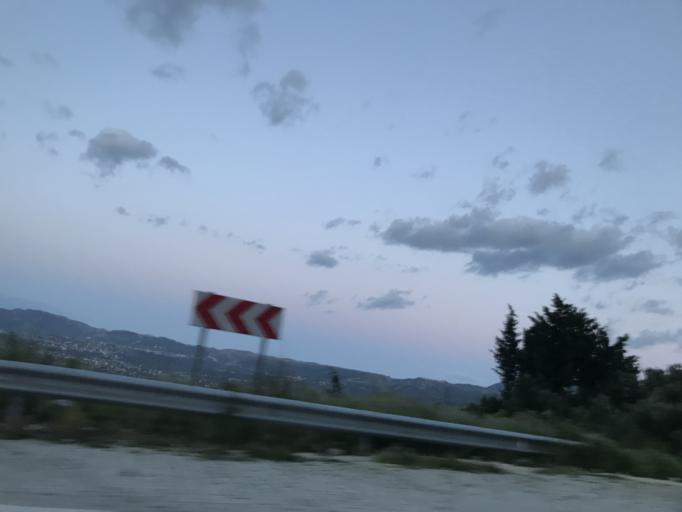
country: TR
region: Hatay
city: Uzunbag
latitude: 36.1201
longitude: 36.0471
